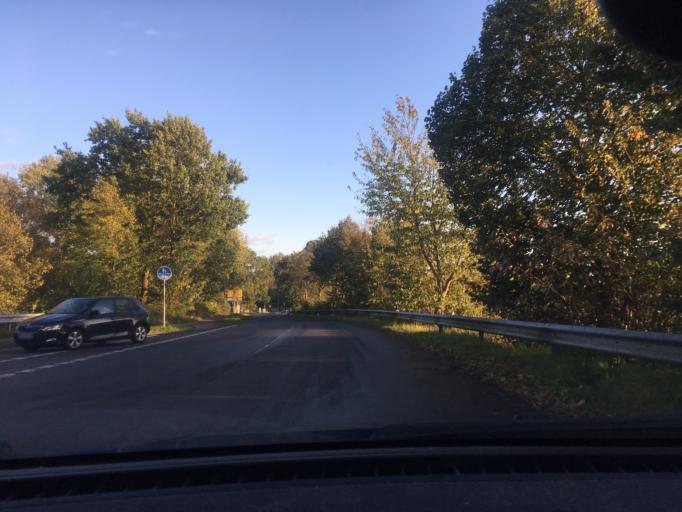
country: DE
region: Lower Saxony
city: Deutsch Evern
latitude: 53.2026
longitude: 10.4313
